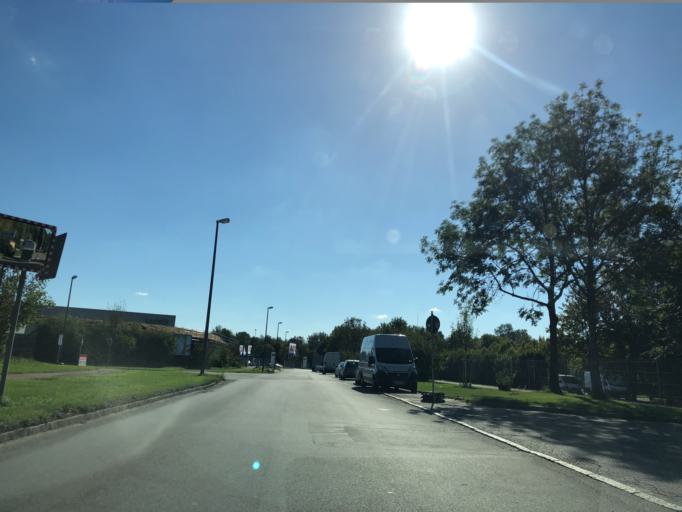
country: DE
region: Baden-Wuerttemberg
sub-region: Tuebingen Region
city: Ulm
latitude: 48.3628
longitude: 9.9537
